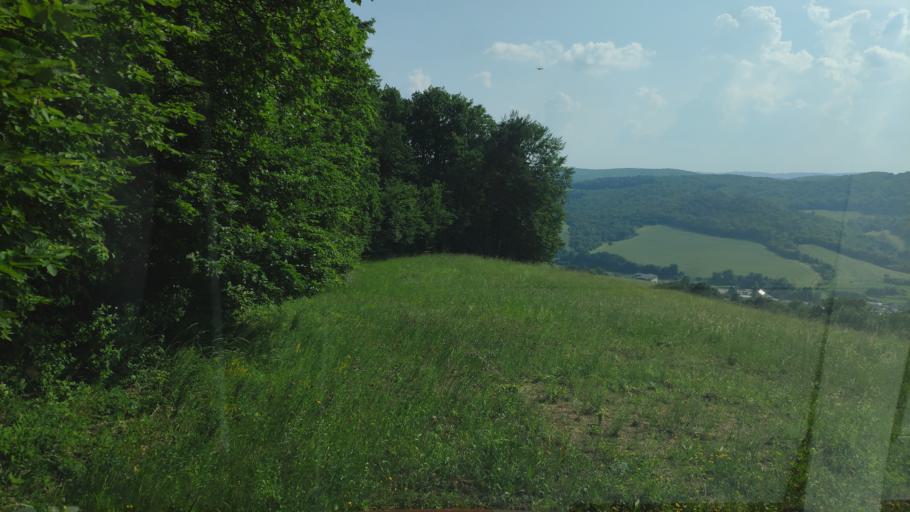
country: SK
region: Presovsky
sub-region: Okres Presov
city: Presov
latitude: 48.9668
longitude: 21.1526
